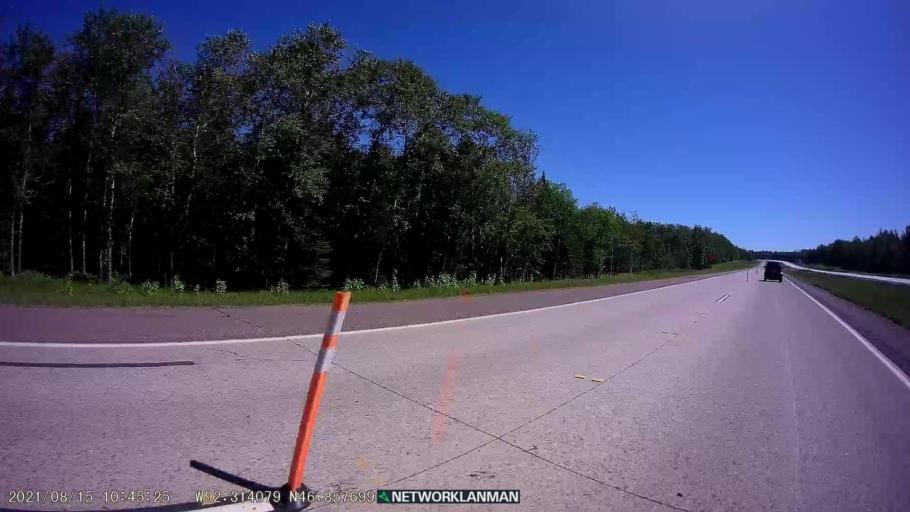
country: US
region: Minnesota
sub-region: Saint Louis County
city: Hermantown
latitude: 46.8576
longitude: -92.3137
